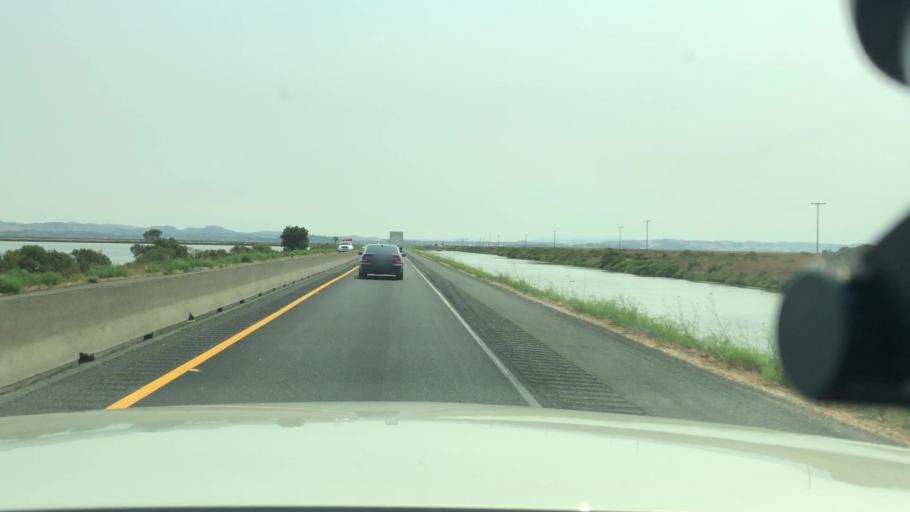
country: US
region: California
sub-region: Napa County
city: American Canyon
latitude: 38.1408
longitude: -122.3609
